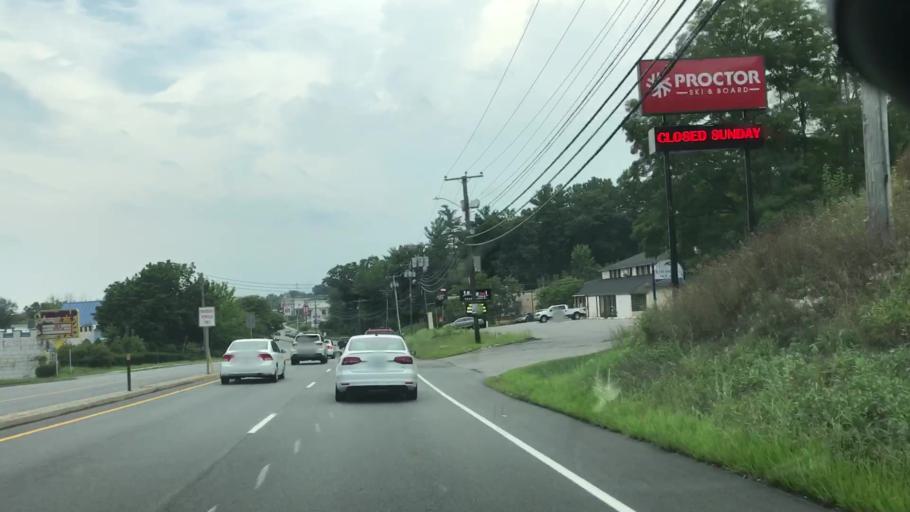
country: US
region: Massachusetts
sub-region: Middlesex County
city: Tyngsboro
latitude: 42.7175
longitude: -71.4427
